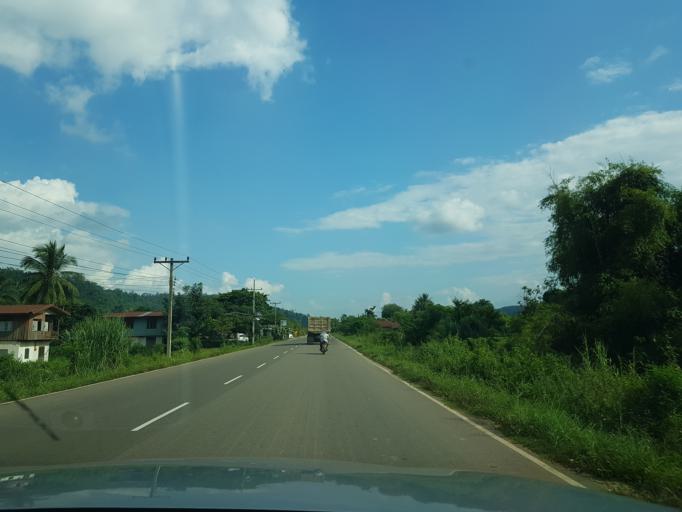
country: TH
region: Nong Khai
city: Sangkhom
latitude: 18.0212
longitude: 102.3906
